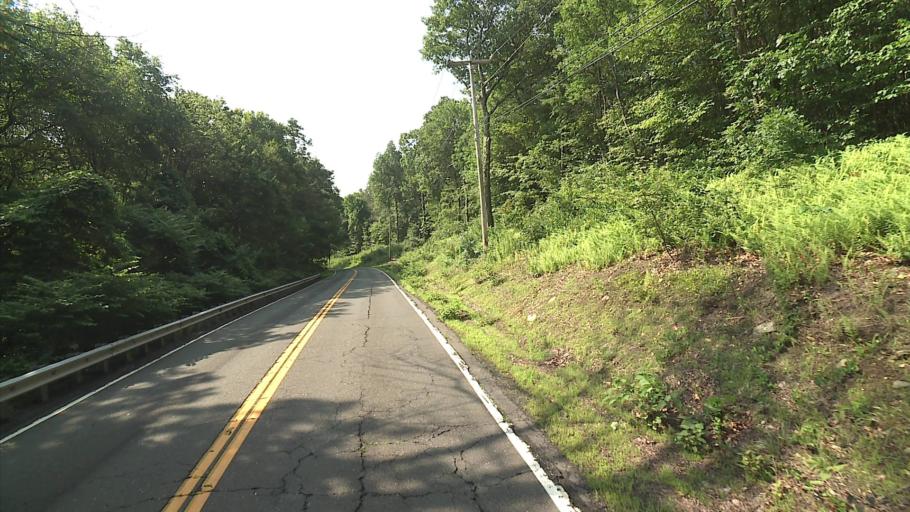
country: US
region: Connecticut
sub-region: New Haven County
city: Wolcott
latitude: 41.5789
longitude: -72.9515
